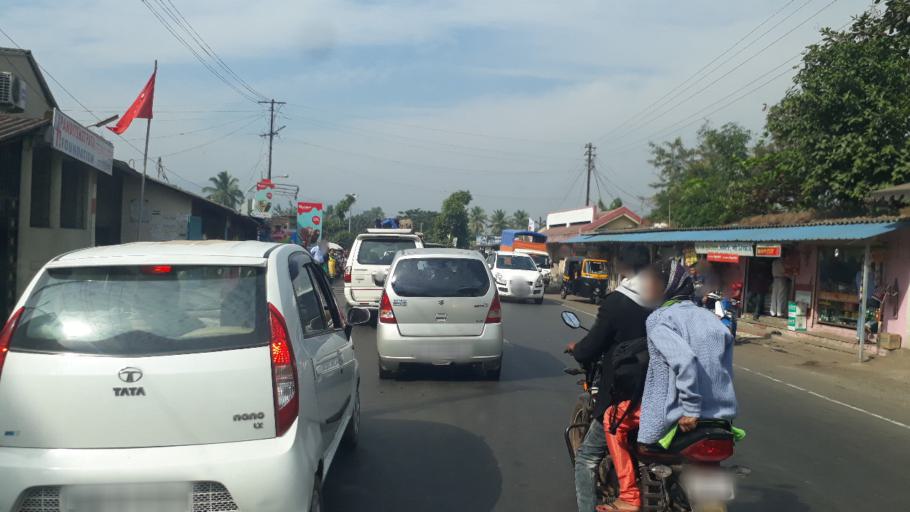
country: IN
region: Maharashtra
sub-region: Raigarh
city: Alibag
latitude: 18.6882
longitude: 72.9866
